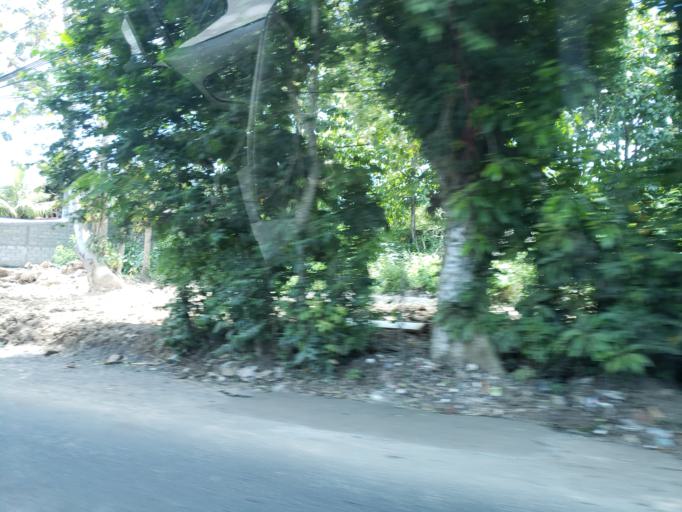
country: ID
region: Bali
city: Kangin
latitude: -8.8205
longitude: 115.1493
